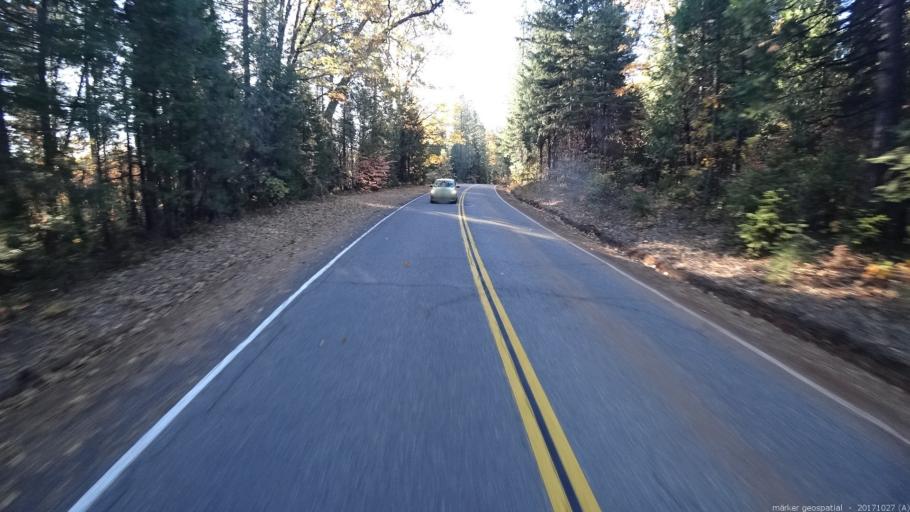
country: US
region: California
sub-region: Shasta County
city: Burney
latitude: 40.9722
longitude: -121.9299
